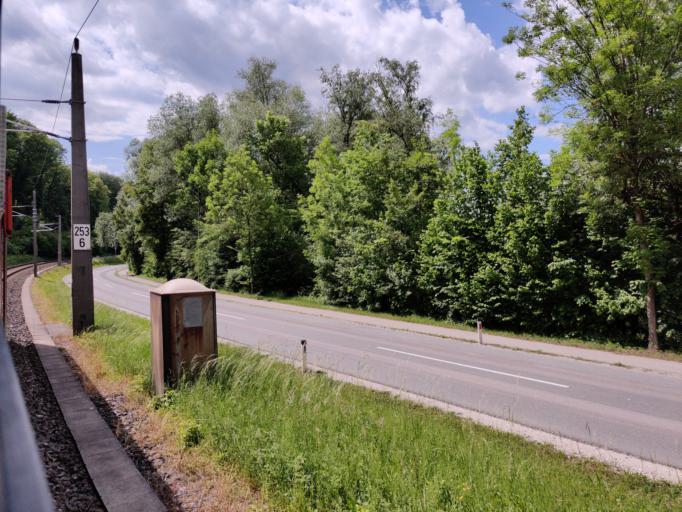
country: AT
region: Styria
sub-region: Politischer Bezirk Leibnitz
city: Ehrenhausen
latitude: 46.7279
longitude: 15.5814
